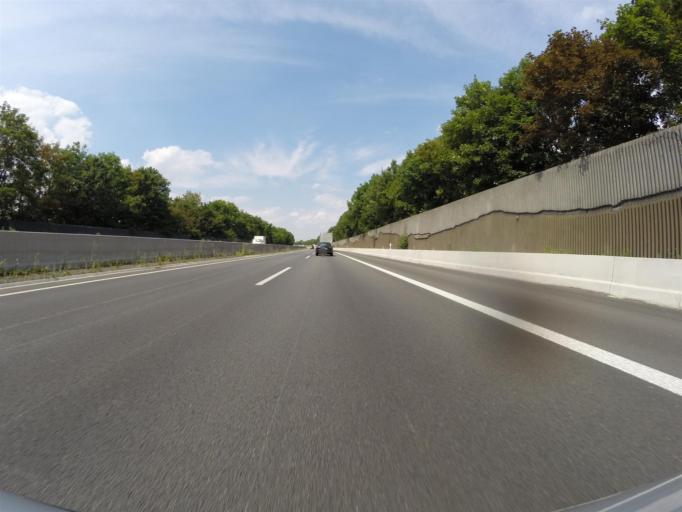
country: DE
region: North Rhine-Westphalia
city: Buende
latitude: 52.1931
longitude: 8.5643
